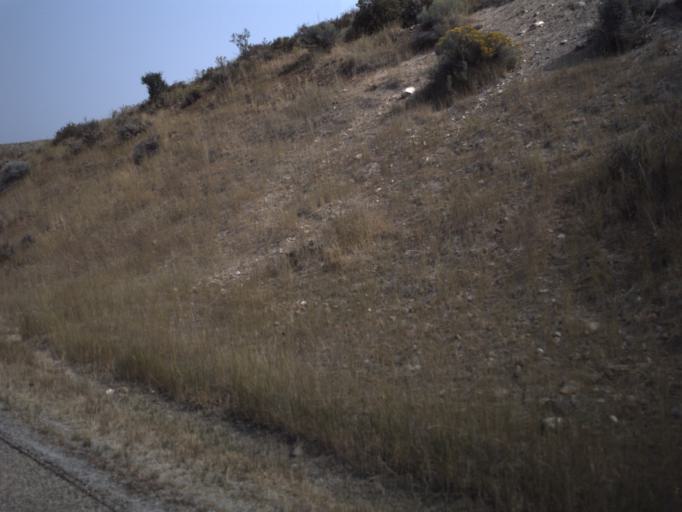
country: US
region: Utah
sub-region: Summit County
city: Summit Park
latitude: 40.8871
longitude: -111.5807
